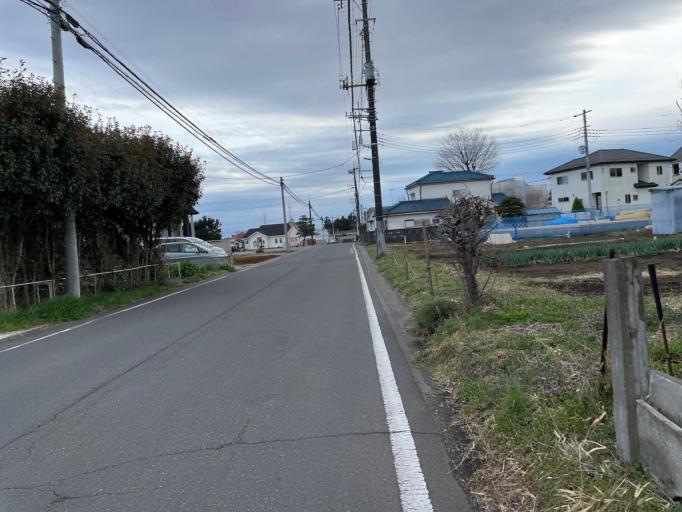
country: JP
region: Saitama
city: Morohongo
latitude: 35.9399
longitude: 139.3466
